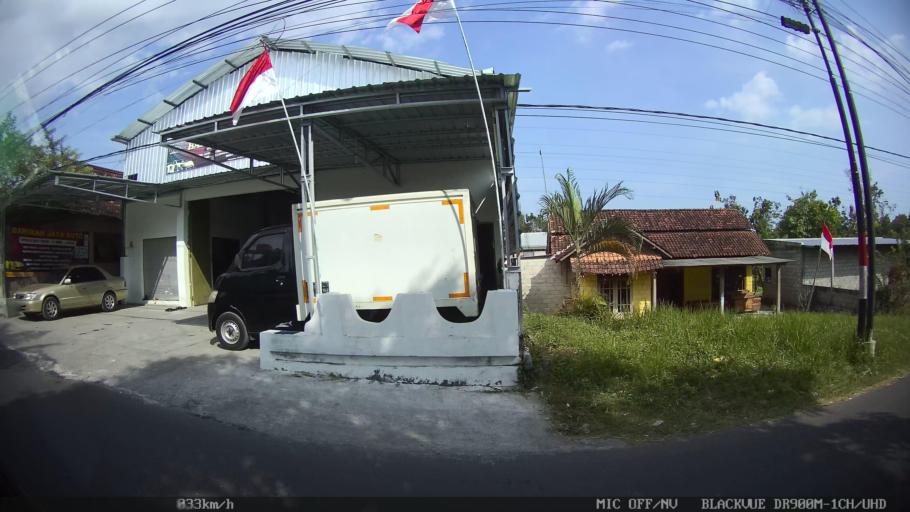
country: ID
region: Daerah Istimewa Yogyakarta
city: Kasihan
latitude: -7.8405
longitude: 110.3126
